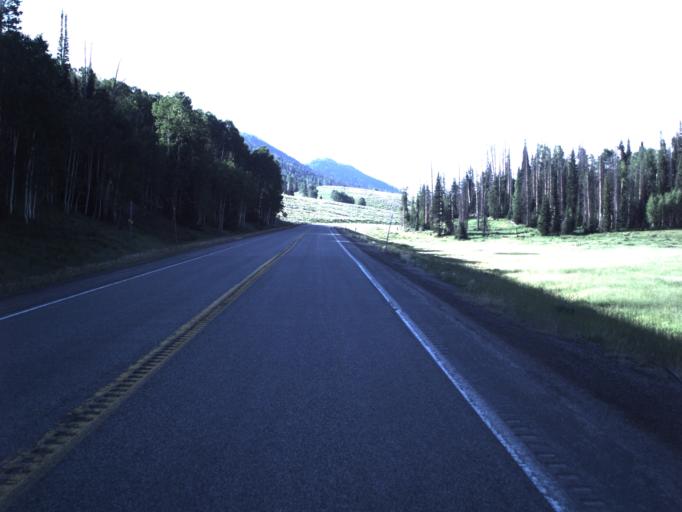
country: US
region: Utah
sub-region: Sanpete County
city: Fairview
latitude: 39.5932
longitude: -111.2281
